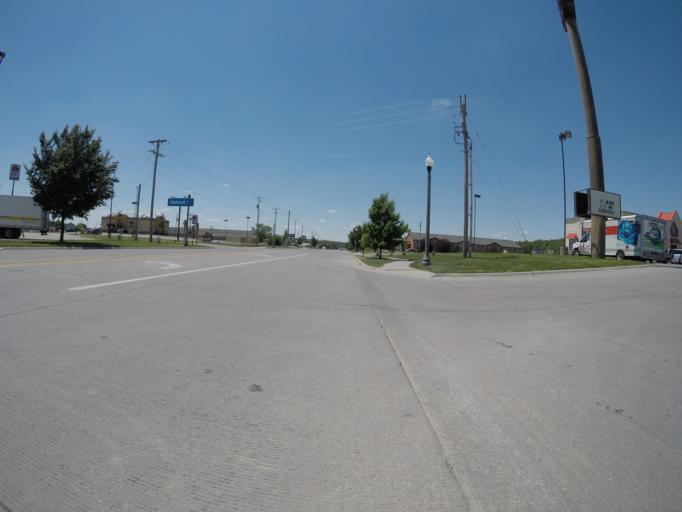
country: US
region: Kansas
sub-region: Geary County
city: Junction City
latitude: 39.0218
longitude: -96.8186
